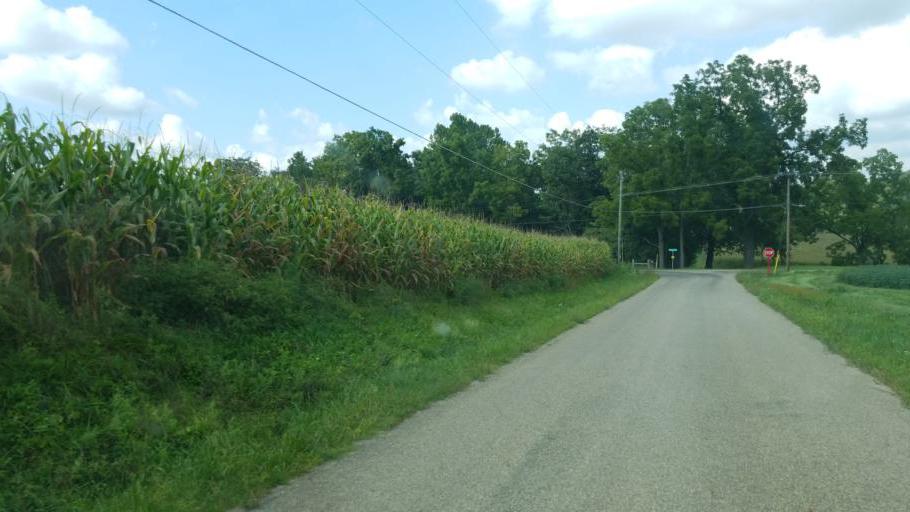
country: US
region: Ohio
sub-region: Knox County
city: Danville
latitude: 40.3996
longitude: -82.3100
